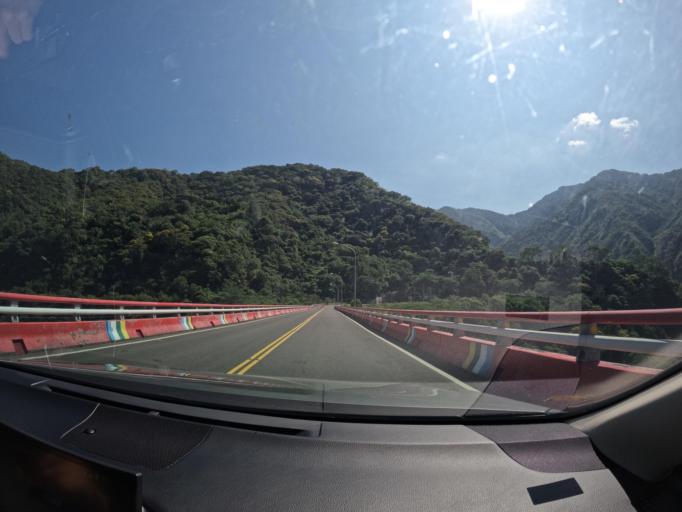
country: TW
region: Taiwan
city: Yujing
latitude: 23.1374
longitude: 120.7289
